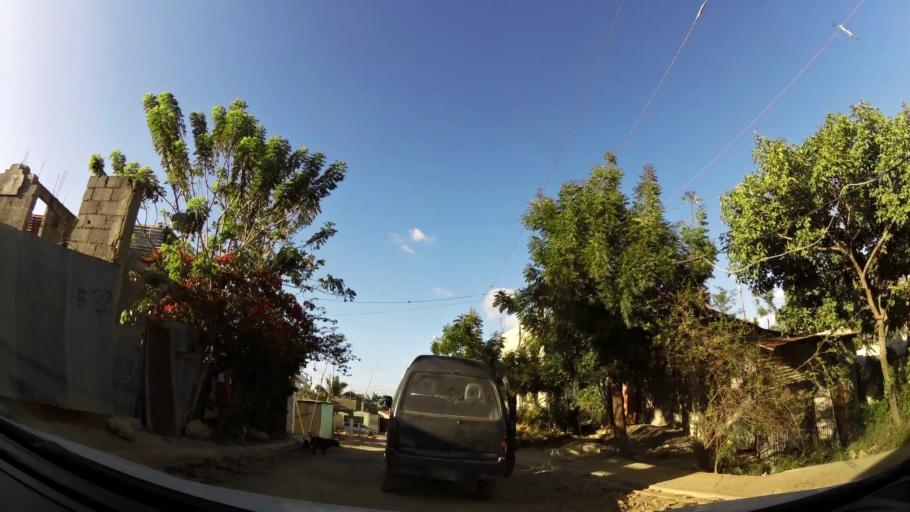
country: DO
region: Santo Domingo
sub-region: Santo Domingo
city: Santo Domingo Este
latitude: 18.4780
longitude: -69.8033
